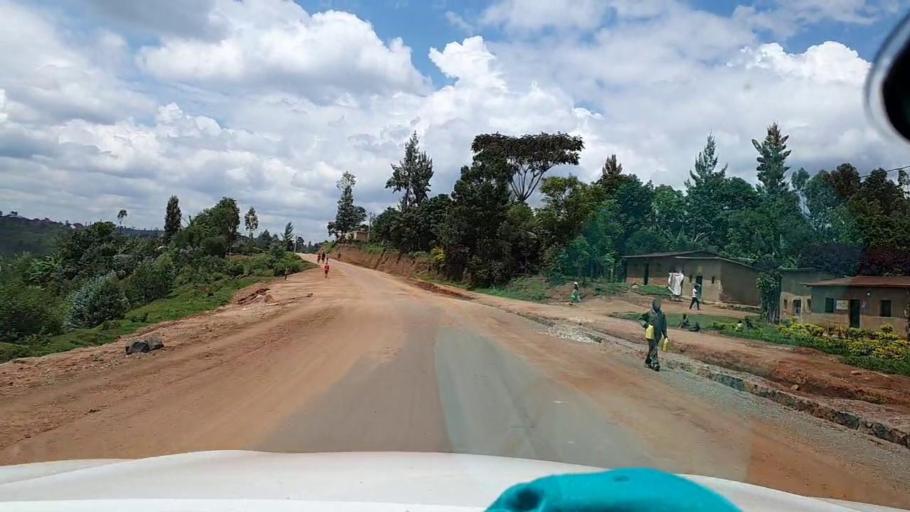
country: RW
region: Southern Province
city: Nzega
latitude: -2.6468
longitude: 29.5658
